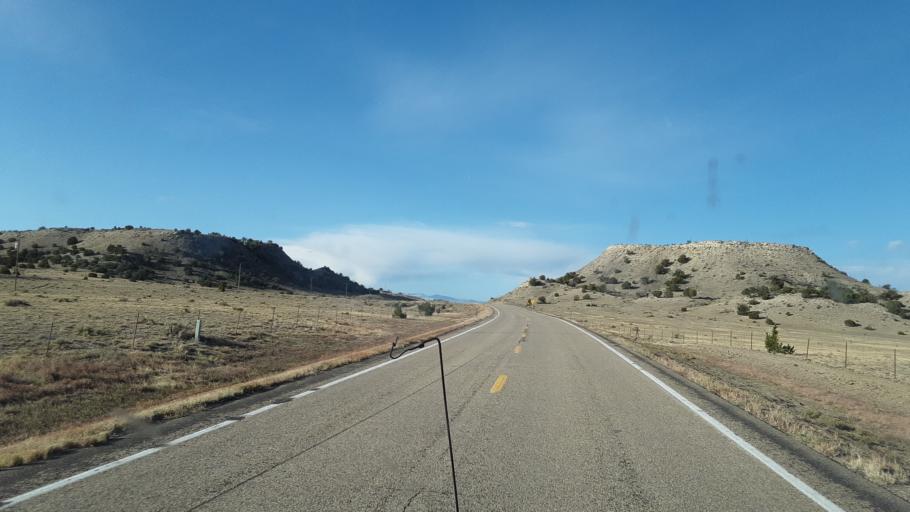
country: US
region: Colorado
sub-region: Huerfano County
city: Walsenburg
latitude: 37.6941
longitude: -104.6276
